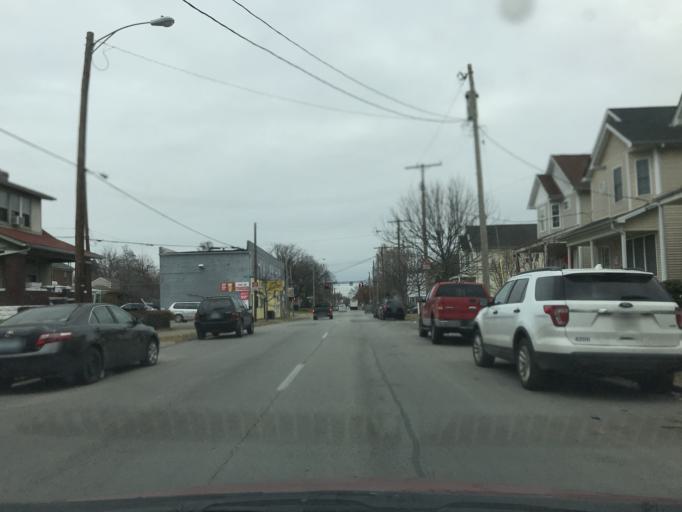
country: US
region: Kentucky
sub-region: Jefferson County
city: Louisville
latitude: 38.2534
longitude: -85.7858
